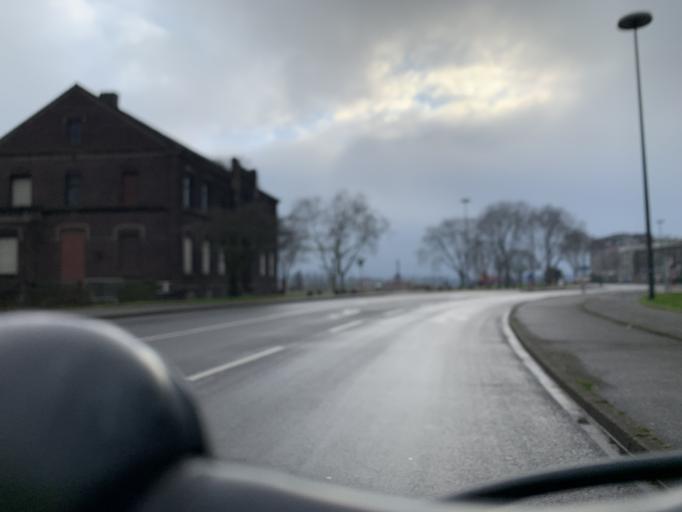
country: DE
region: North Rhine-Westphalia
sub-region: Regierungsbezirk Dusseldorf
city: Krefeld
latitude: 51.3699
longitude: 6.6644
